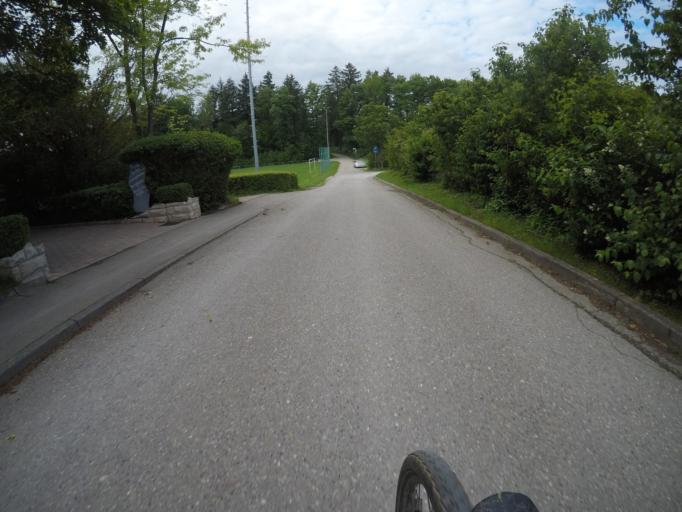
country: DE
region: Baden-Wuerttemberg
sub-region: Regierungsbezirk Stuttgart
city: Kohlberg
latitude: 48.5513
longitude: 9.3189
